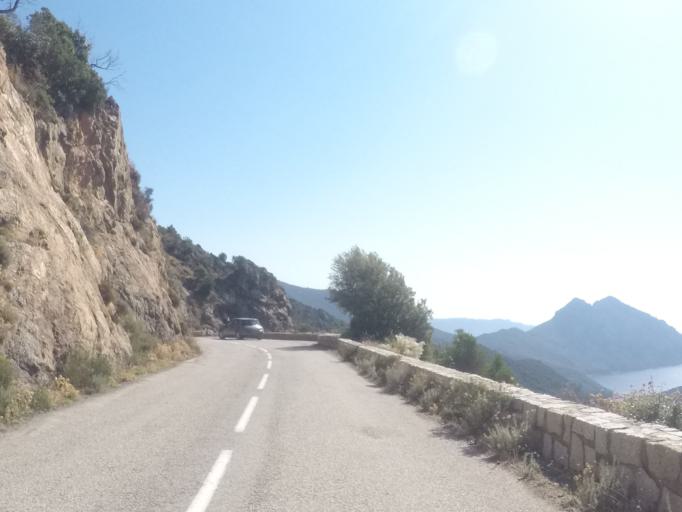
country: FR
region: Corsica
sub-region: Departement de la Haute-Corse
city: Calvi
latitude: 42.3631
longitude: 8.6483
